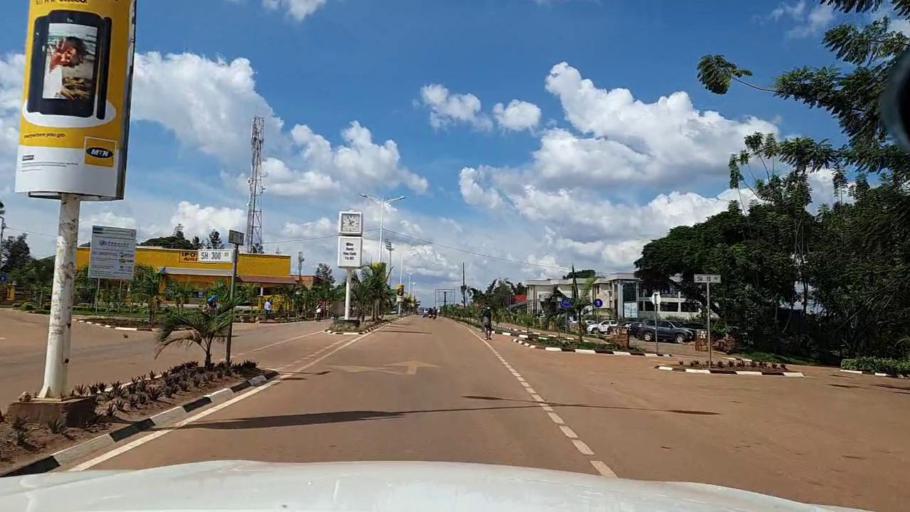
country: RW
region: Southern Province
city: Butare
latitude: -2.6007
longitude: 29.7419
